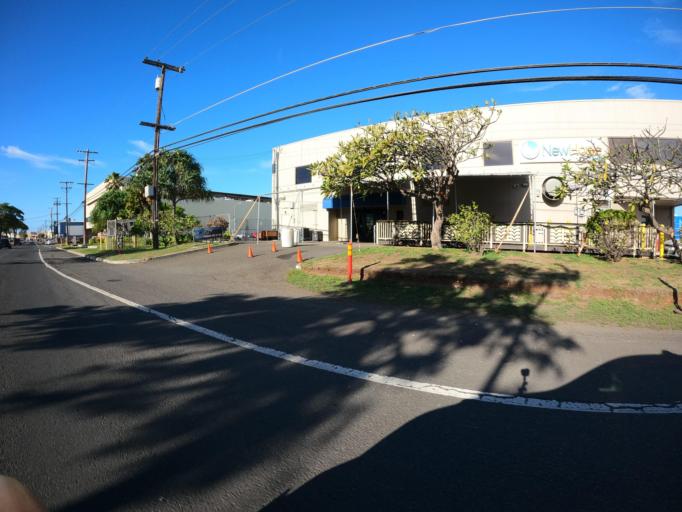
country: US
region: Hawaii
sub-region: Honolulu County
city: Honolulu
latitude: 21.3269
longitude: -157.8884
